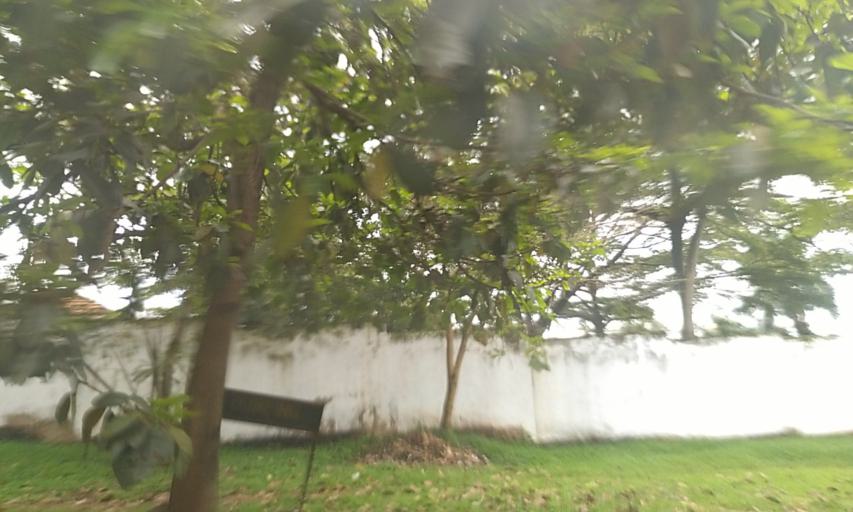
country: UG
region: Central Region
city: Kampala Central Division
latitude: 0.3309
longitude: 32.5897
